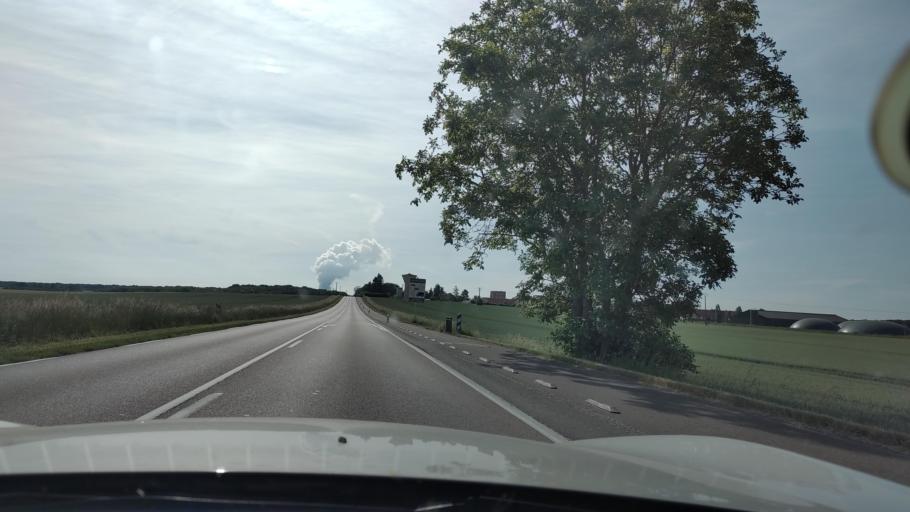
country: FR
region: Ile-de-France
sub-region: Departement de Seine-et-Marne
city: Sourdun
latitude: 48.5351
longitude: 3.3635
